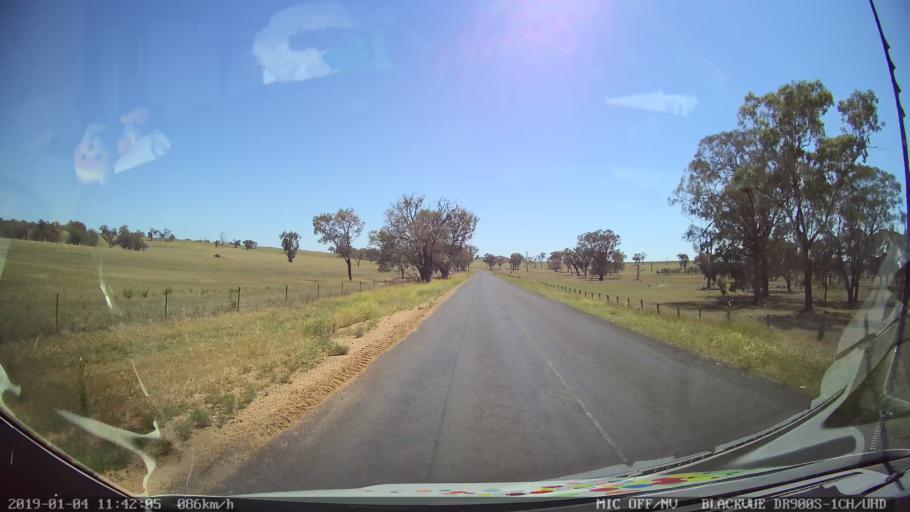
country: AU
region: New South Wales
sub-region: Cabonne
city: Molong
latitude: -32.9859
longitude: 148.7866
